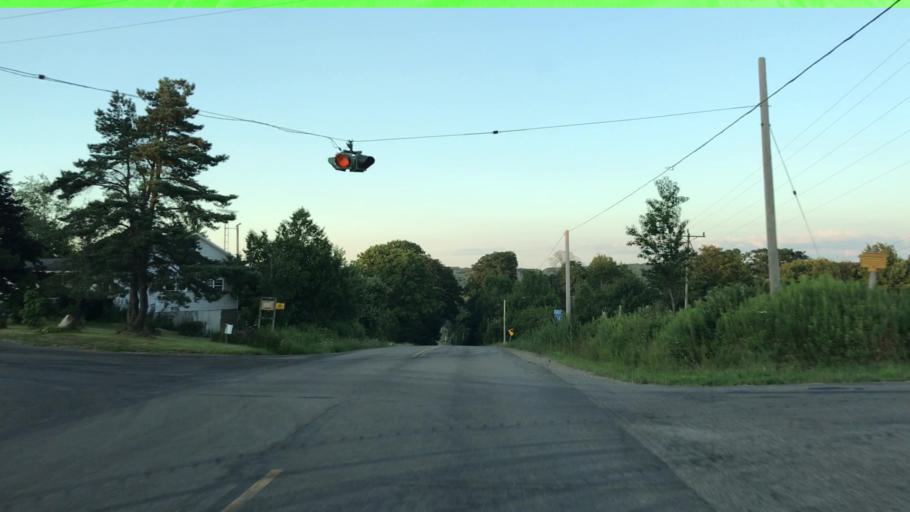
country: US
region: New York
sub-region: Chautauqua County
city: Mayville
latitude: 42.2807
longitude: -79.4422
